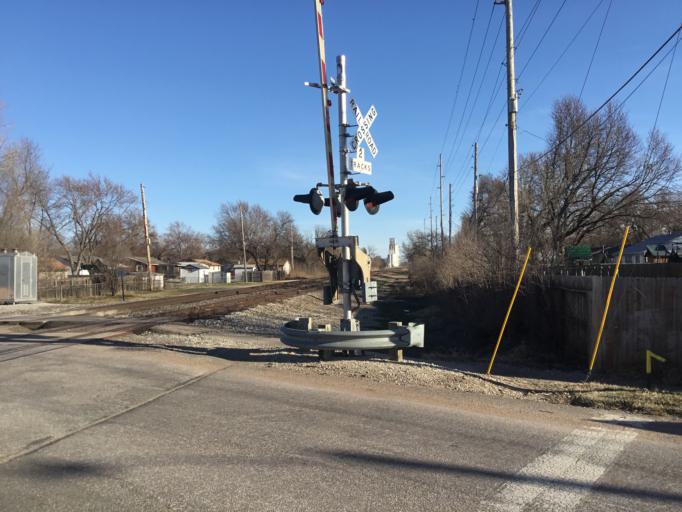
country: US
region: Kansas
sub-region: Sedgwick County
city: Valley Center
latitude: 37.8395
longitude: -97.3801
